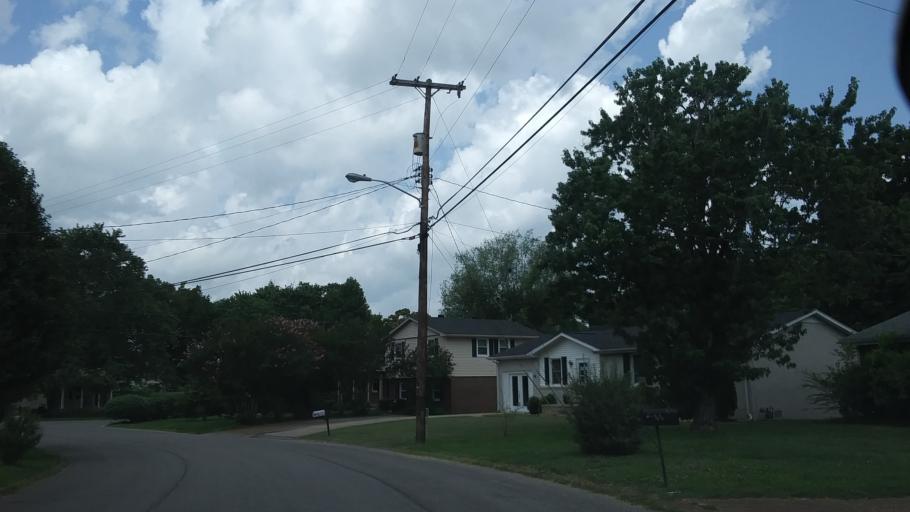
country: US
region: Tennessee
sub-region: Davidson County
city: Belle Meade
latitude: 36.1413
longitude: -86.8902
